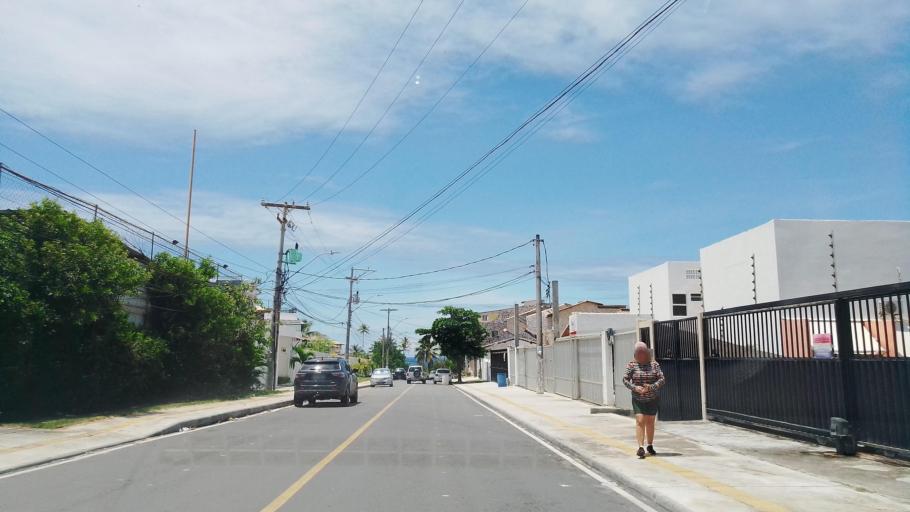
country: BR
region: Bahia
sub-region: Lauro De Freitas
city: Lauro de Freitas
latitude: -12.9333
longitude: -38.3288
